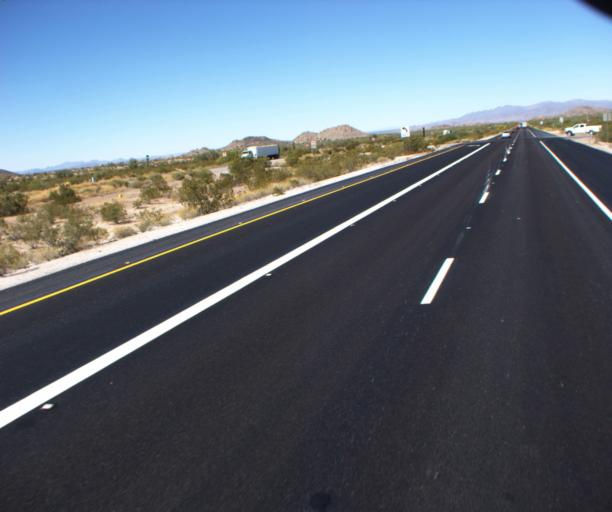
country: US
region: Arizona
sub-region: Maricopa County
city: Buckeye
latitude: 33.2749
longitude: -112.6319
